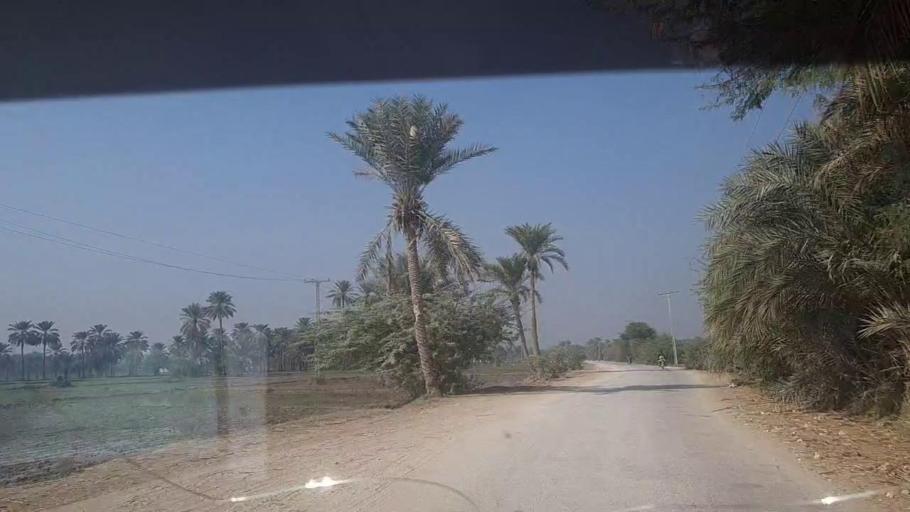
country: PK
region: Sindh
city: Kot Diji
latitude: 27.3600
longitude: 68.7086
